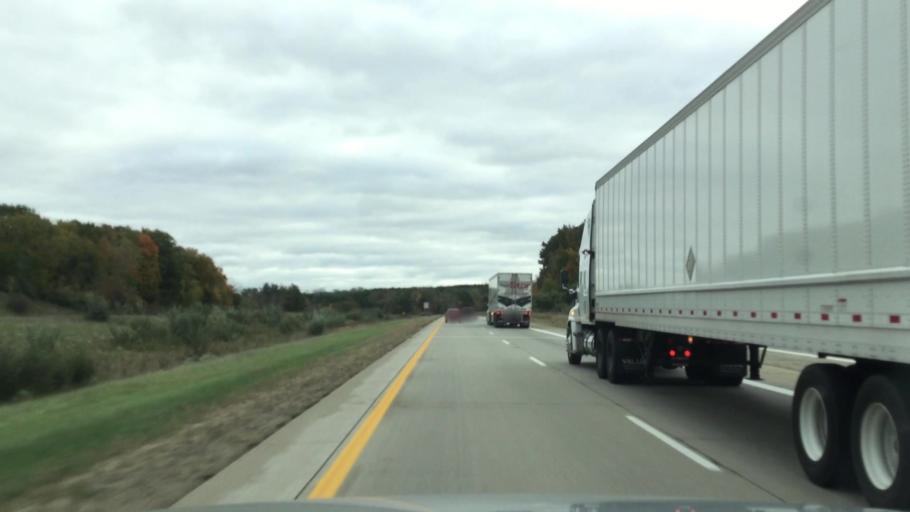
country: US
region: Michigan
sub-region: Lapeer County
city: Lapeer
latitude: 43.0083
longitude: -83.2228
